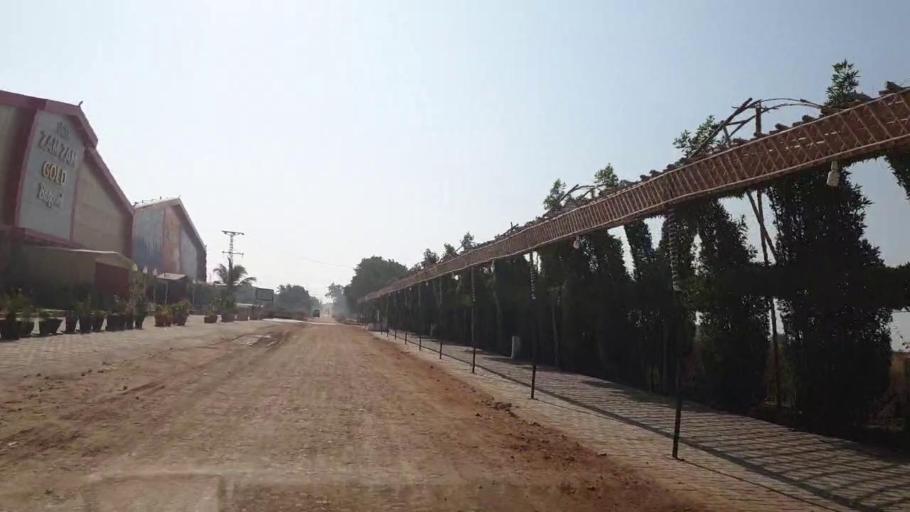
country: PK
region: Sindh
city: Thatta
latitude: 24.7586
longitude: 67.9169
